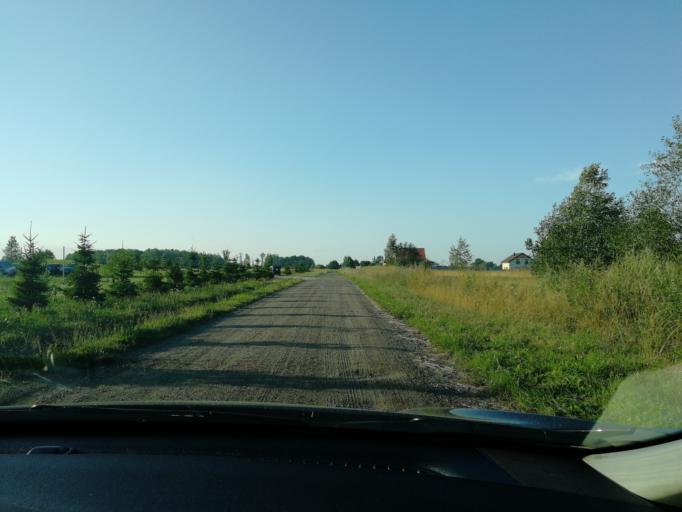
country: LT
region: Klaipedos apskritis
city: Kretinga
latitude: 55.7895
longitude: 21.2219
